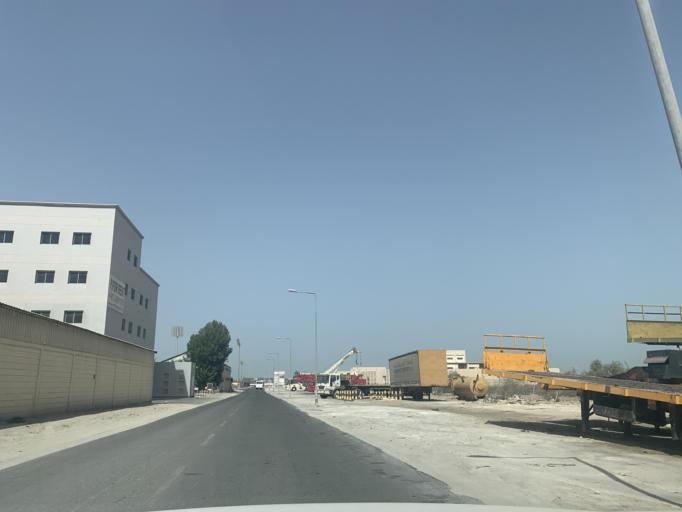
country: BH
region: Northern
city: Sitrah
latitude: 26.1541
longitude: 50.6231
